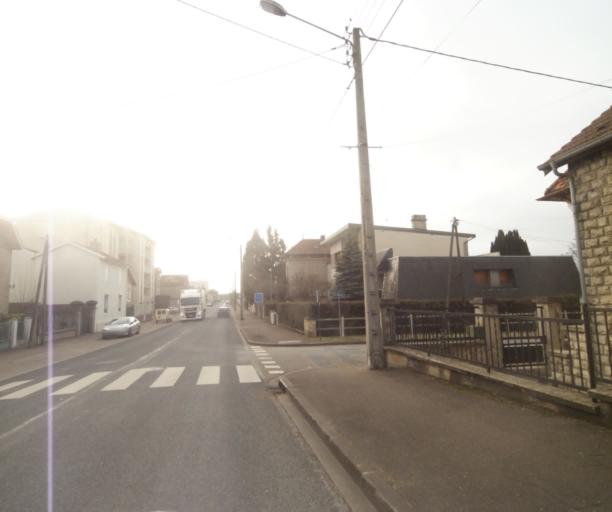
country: FR
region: Champagne-Ardenne
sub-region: Departement de la Haute-Marne
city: Saint-Dizier
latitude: 48.6415
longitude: 4.9333
